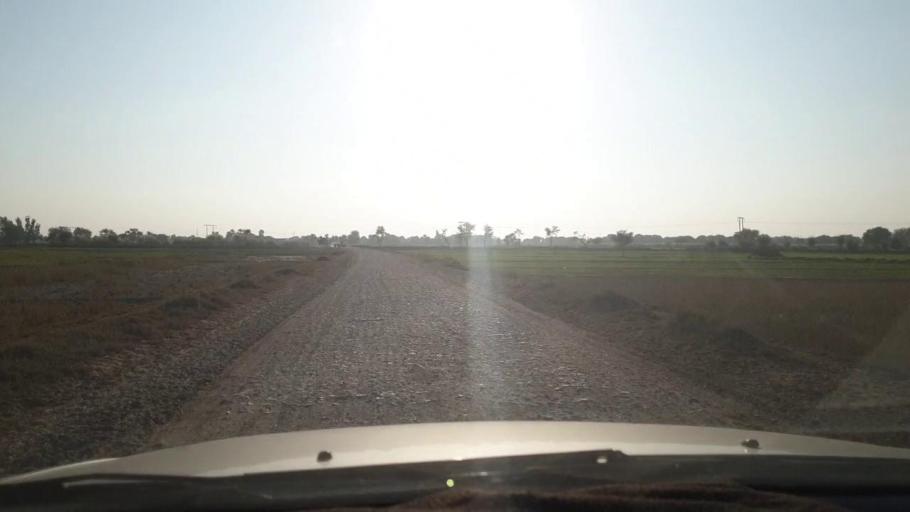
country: PK
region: Sindh
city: Mirpur Mathelo
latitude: 28.0022
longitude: 69.5277
